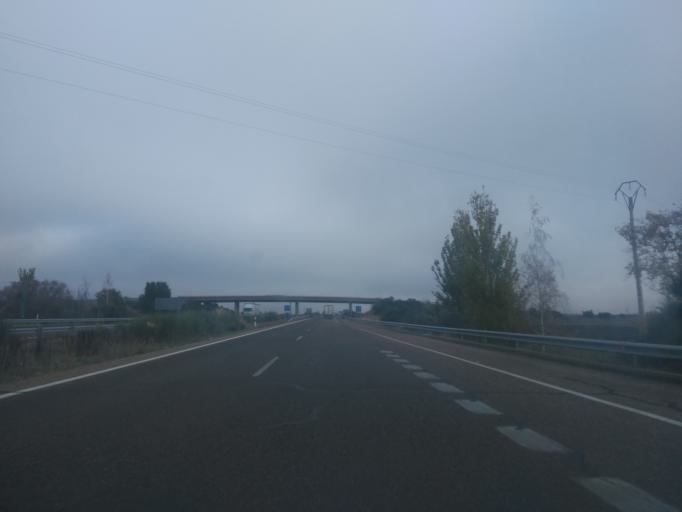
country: ES
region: Castille and Leon
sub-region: Provincia de Salamanca
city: Pedrosillo el Ralo
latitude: 41.0608
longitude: -5.5397
